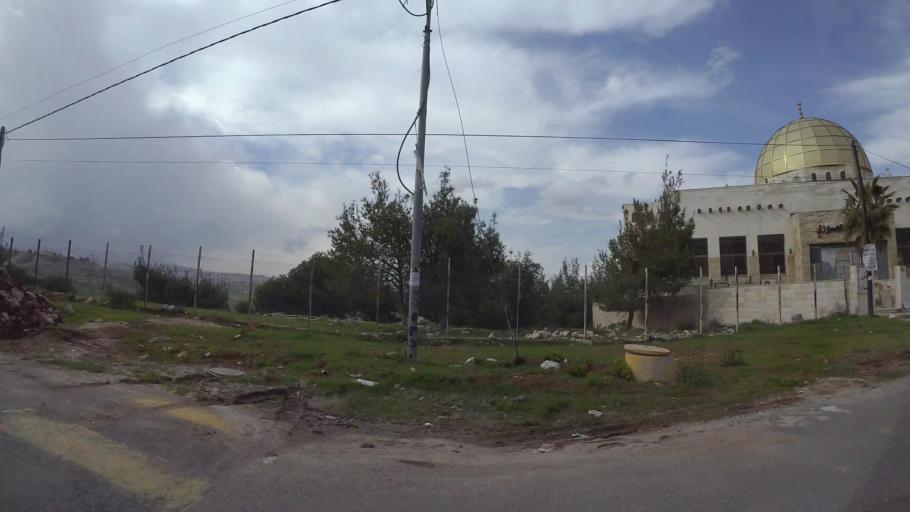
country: JO
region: Amman
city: Amman
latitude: 32.0154
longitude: 35.9396
